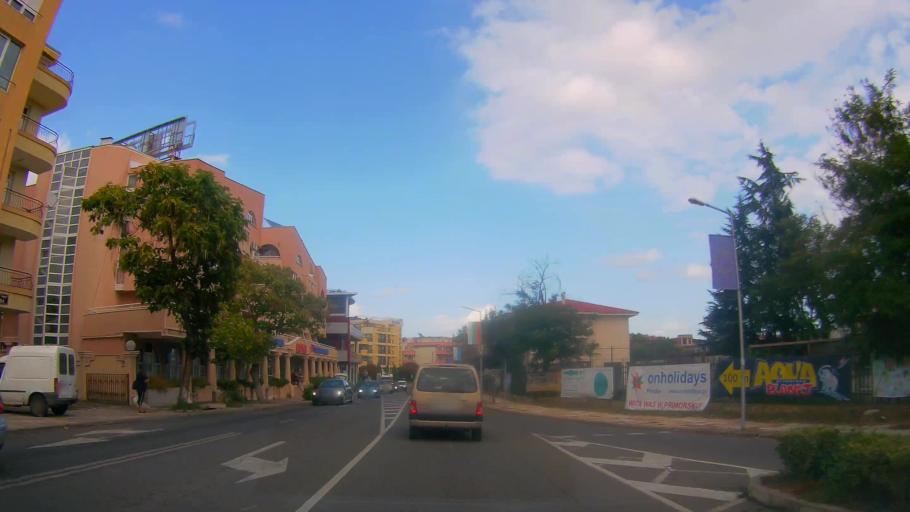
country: BG
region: Burgas
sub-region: Obshtina Primorsko
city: Primorsko
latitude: 42.2660
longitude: 27.7479
